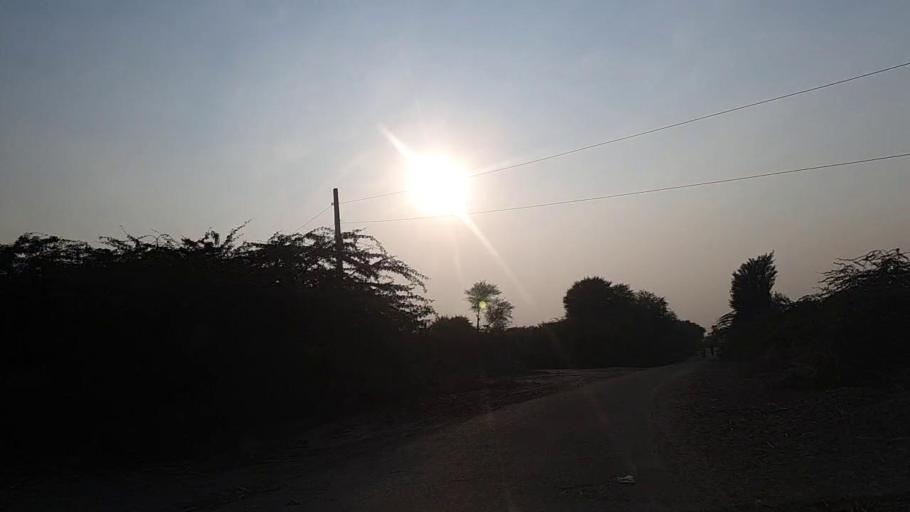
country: PK
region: Sindh
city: Jam Sahib
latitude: 26.4303
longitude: 68.5858
